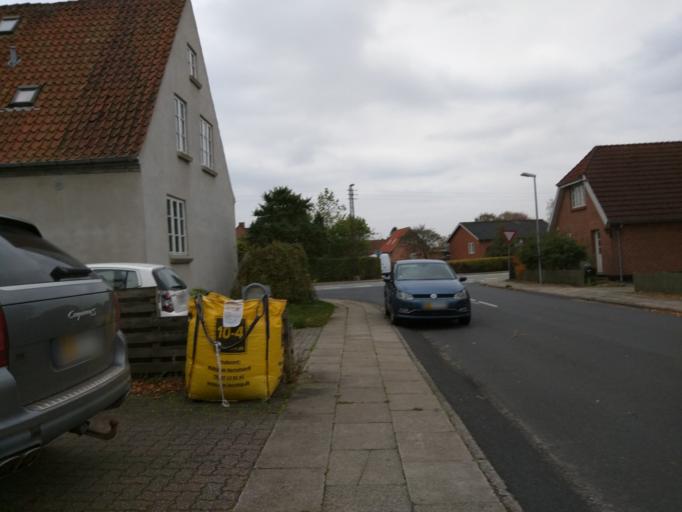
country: DK
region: Central Jutland
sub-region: Viborg Kommune
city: Viborg
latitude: 56.4548
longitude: 9.3889
